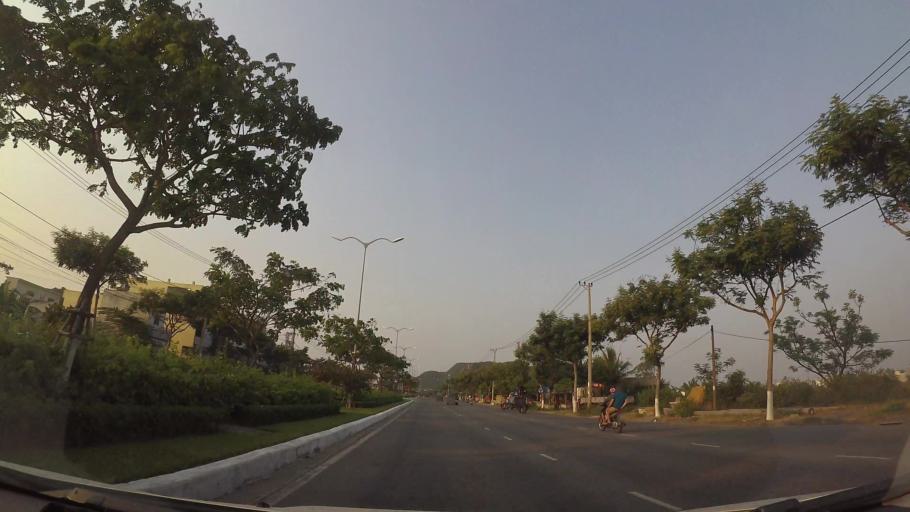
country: VN
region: Da Nang
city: Ngu Hanh Son
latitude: 15.9948
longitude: 108.2589
